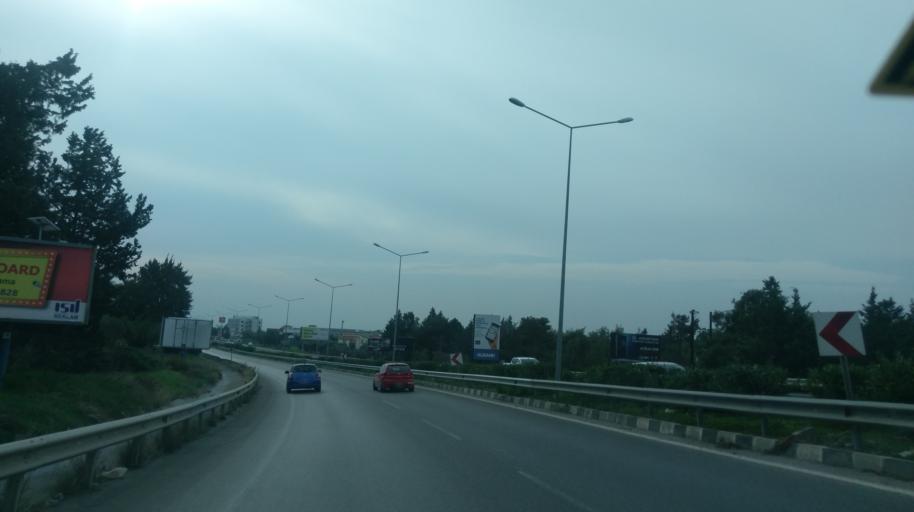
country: CY
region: Keryneia
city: Kyrenia
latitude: 35.2902
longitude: 33.2763
